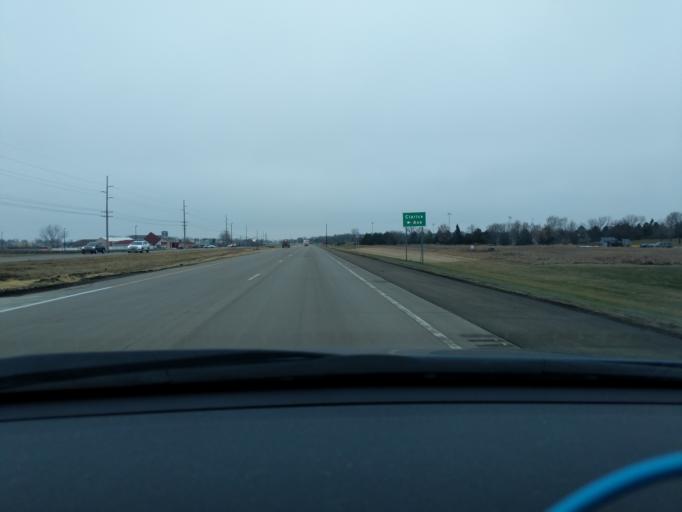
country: US
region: Minnesota
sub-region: Lyon County
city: Marshall
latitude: 44.4425
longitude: -95.7633
